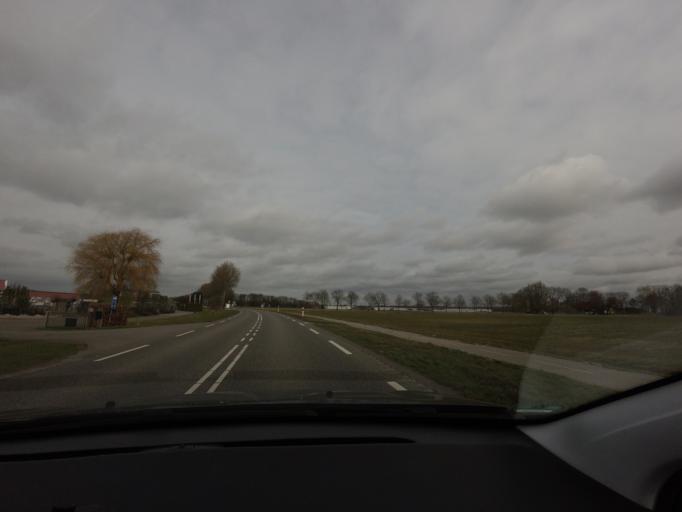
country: NL
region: Friesland
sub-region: Gemeente Lemsterland
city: Lemmer
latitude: 52.8329
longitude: 5.7111
